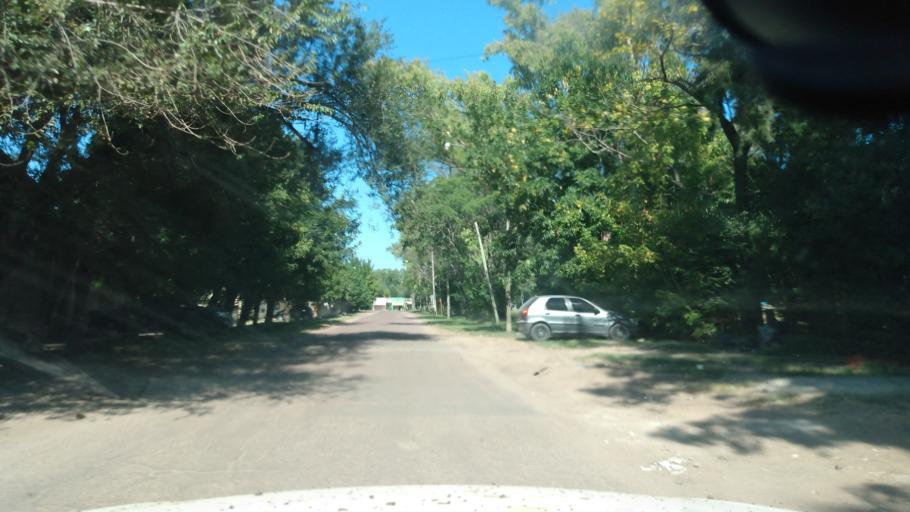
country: AR
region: Buenos Aires
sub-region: Partido de Lujan
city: Lujan
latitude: -34.4888
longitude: -59.0767
